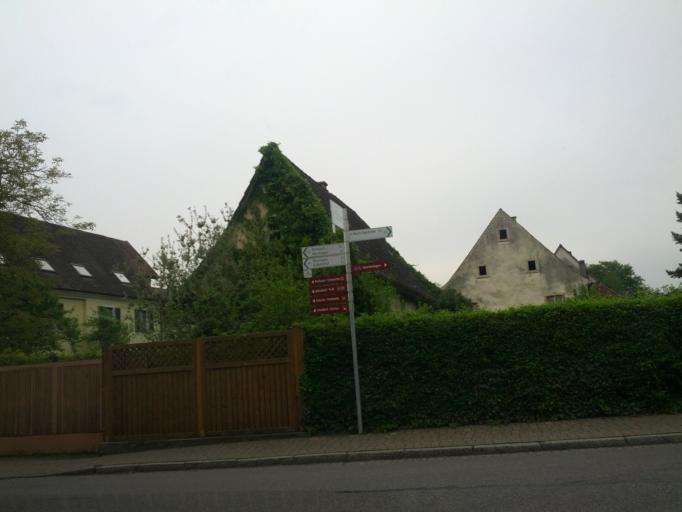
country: DE
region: Baden-Wuerttemberg
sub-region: Freiburg Region
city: Gottenheim
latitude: 48.0510
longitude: 7.7308
